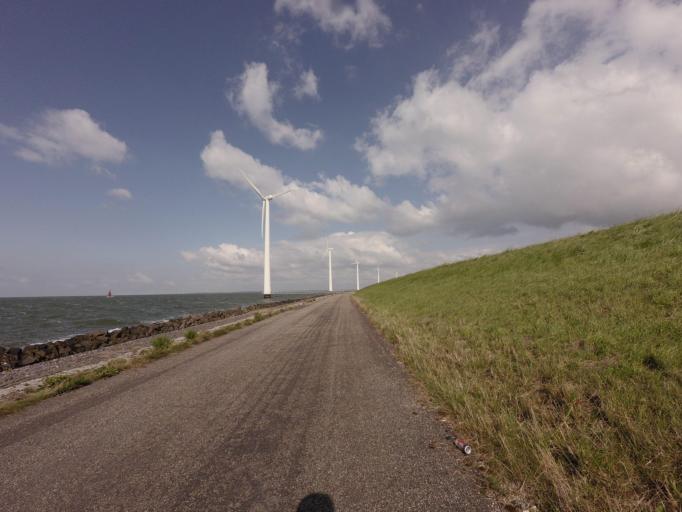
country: NL
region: Flevoland
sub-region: Gemeente Urk
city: Urk
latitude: 52.5905
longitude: 5.5560
